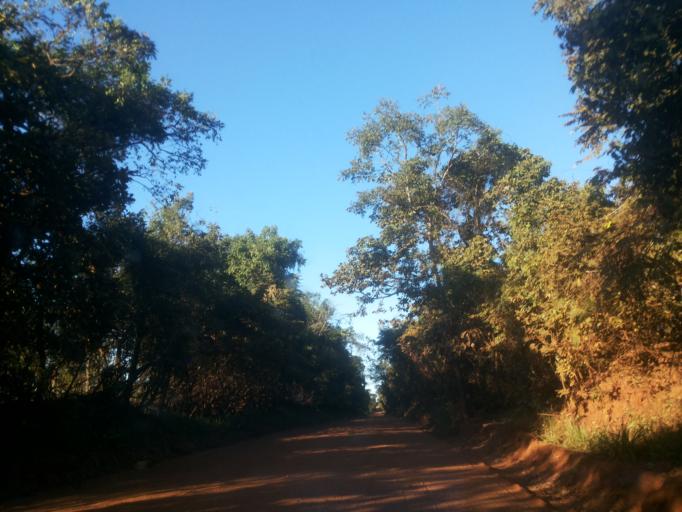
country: BR
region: Minas Gerais
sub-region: Campina Verde
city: Campina Verde
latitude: -19.3065
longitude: -49.7566
